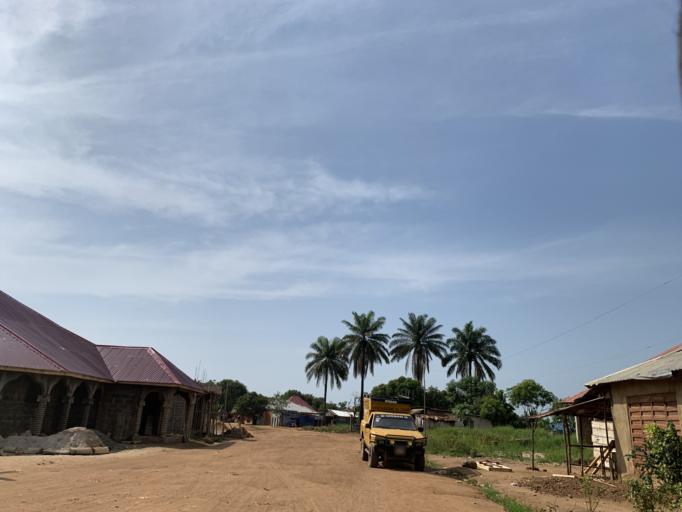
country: SL
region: Western Area
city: Waterloo
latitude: 8.3428
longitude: -13.0481
